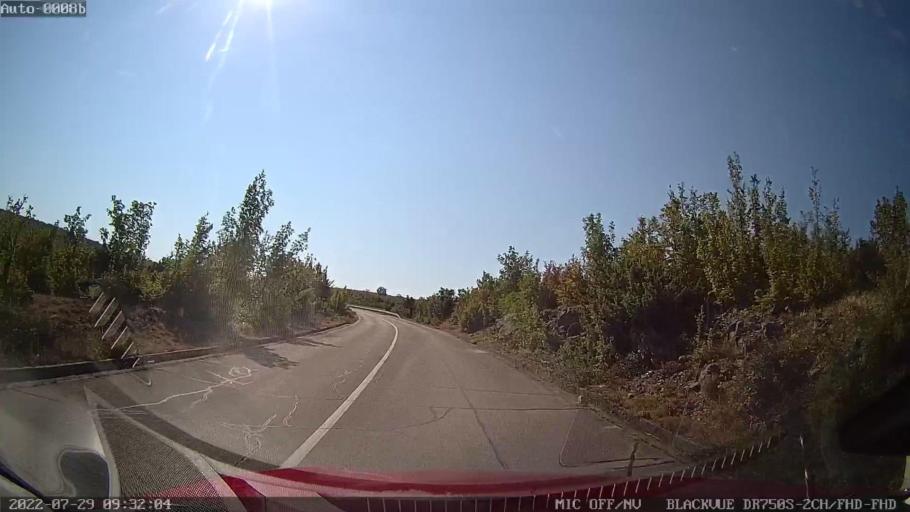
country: HR
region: Zadarska
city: Obrovac
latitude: 44.1843
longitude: 15.7064
